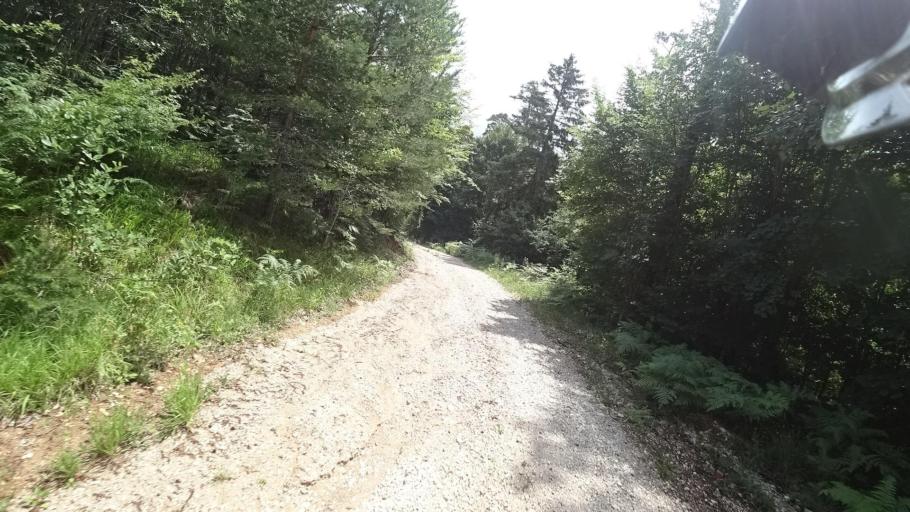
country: HR
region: Licko-Senjska
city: Otocac
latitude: 44.8732
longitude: 15.4246
